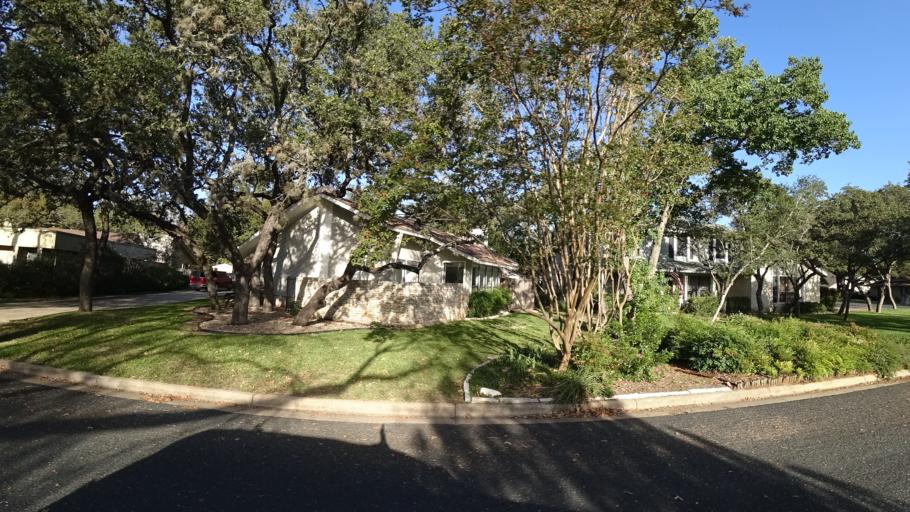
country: US
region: Texas
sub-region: Williamson County
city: Anderson Mill
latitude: 30.4314
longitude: -97.8069
